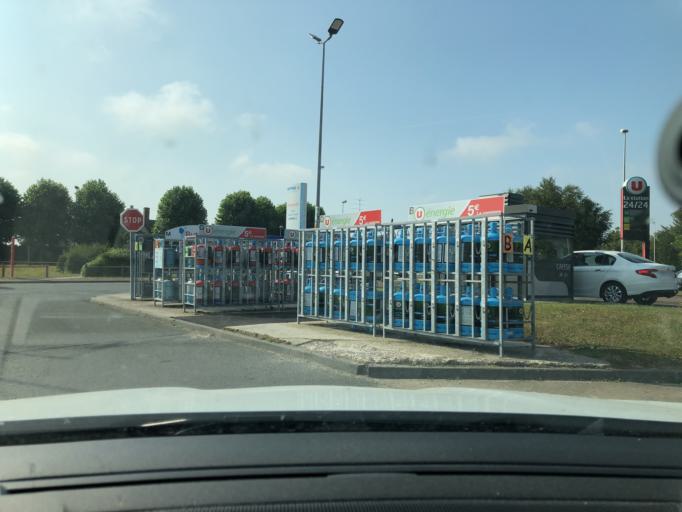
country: FR
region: Lower Normandy
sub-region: Departement du Calvados
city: Douvres-la-Delivrande
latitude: 49.3003
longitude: -0.3814
